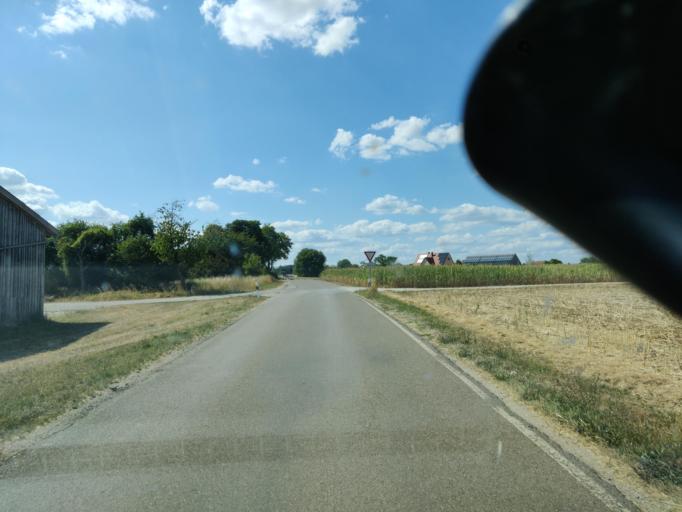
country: DE
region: Bavaria
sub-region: Regierungsbezirk Mittelfranken
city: Thalmassing
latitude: 49.0659
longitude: 11.2279
